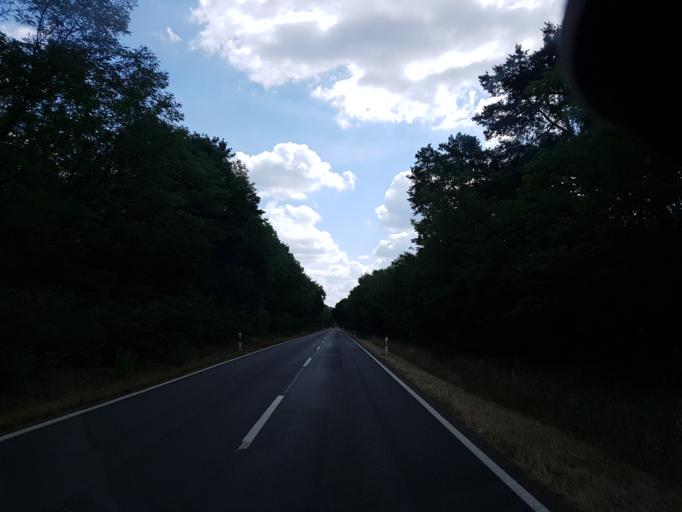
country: DE
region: Brandenburg
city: Altdobern
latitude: 51.6880
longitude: 14.1054
